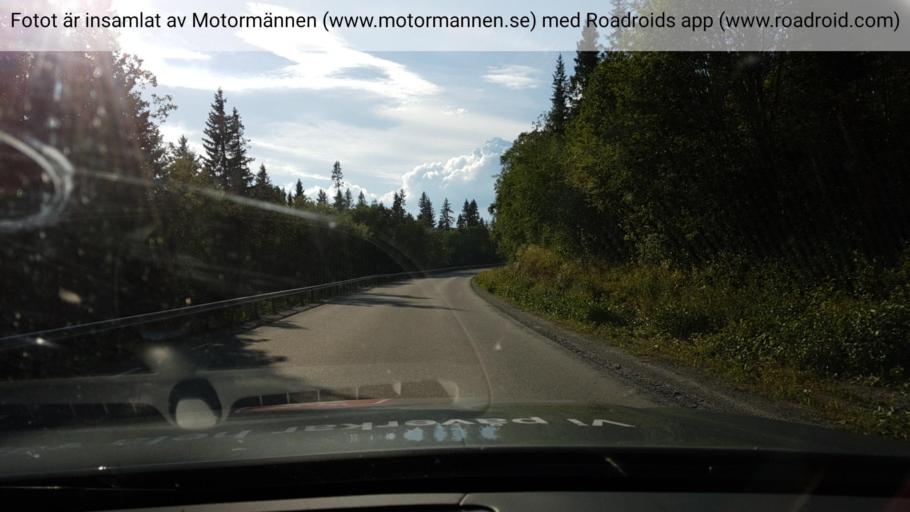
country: SE
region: Jaemtland
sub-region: Are Kommun
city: Are
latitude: 63.4106
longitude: 13.0429
